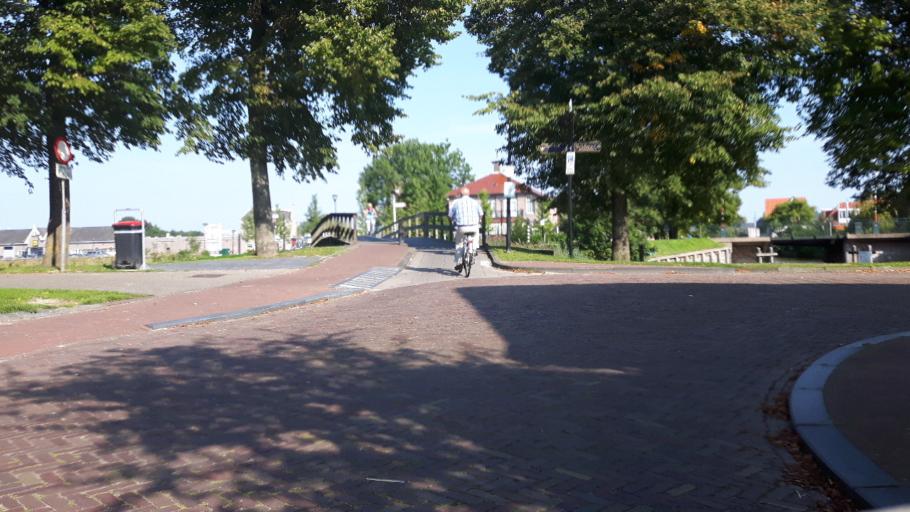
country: NL
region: Friesland
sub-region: Gemeente Franekeradeel
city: Franeker
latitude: 53.1866
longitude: 5.5482
